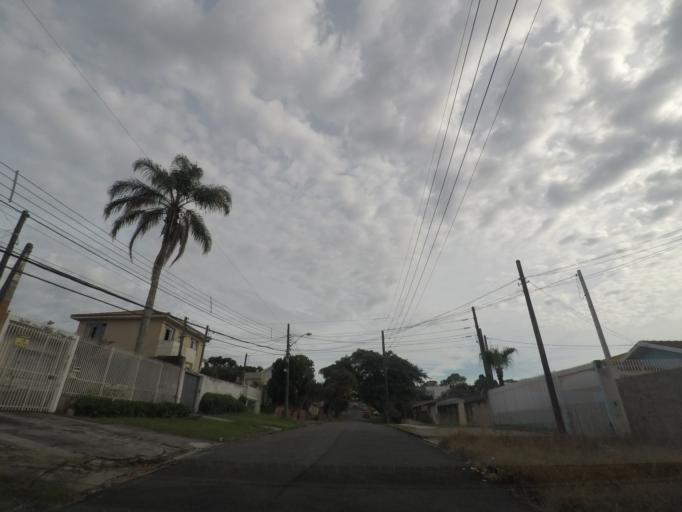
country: BR
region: Parana
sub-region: Curitiba
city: Curitiba
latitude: -25.4209
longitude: -49.2975
